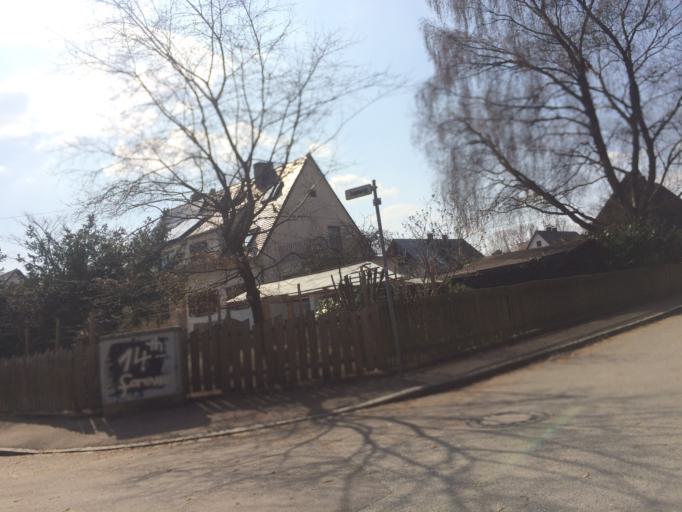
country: DE
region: Bavaria
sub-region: Swabia
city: Gersthofen
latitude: 48.4112
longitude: 10.8943
